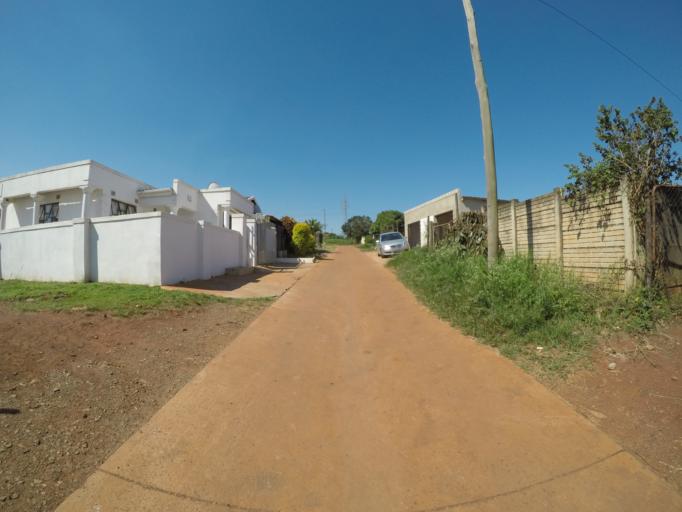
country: ZA
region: KwaZulu-Natal
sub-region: uThungulu District Municipality
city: Empangeni
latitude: -28.7749
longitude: 31.8778
